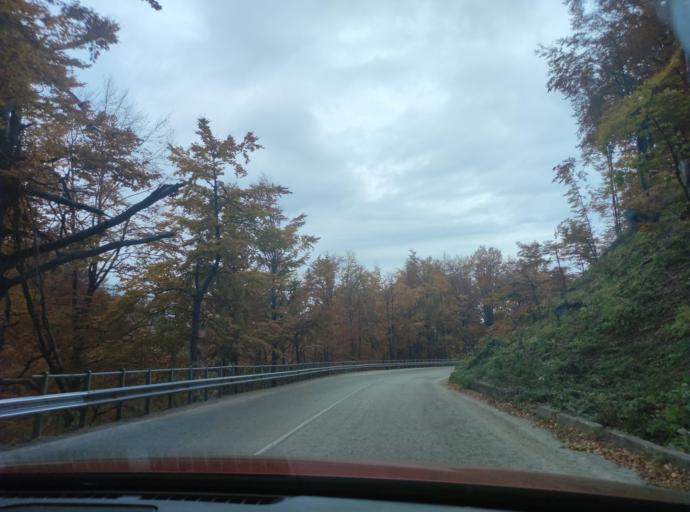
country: BG
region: Montana
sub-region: Obshtina Berkovitsa
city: Berkovitsa
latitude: 43.1271
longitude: 23.1398
